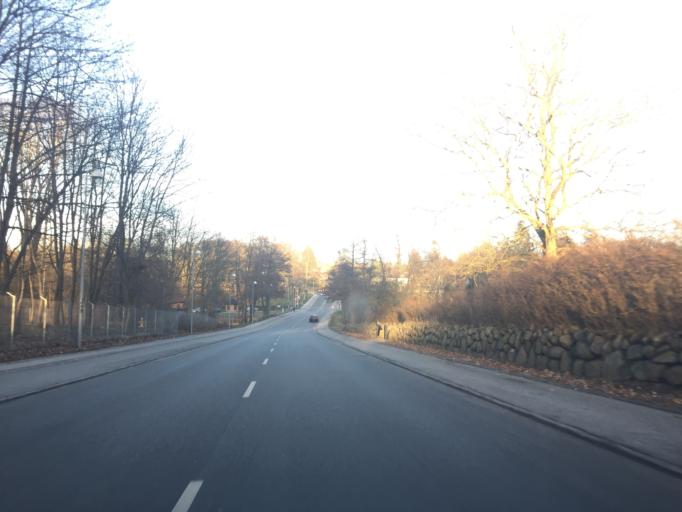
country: DK
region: Capital Region
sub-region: Lyngby-Tarbaek Kommune
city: Kongens Lyngby
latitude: 55.7842
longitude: 12.4939
